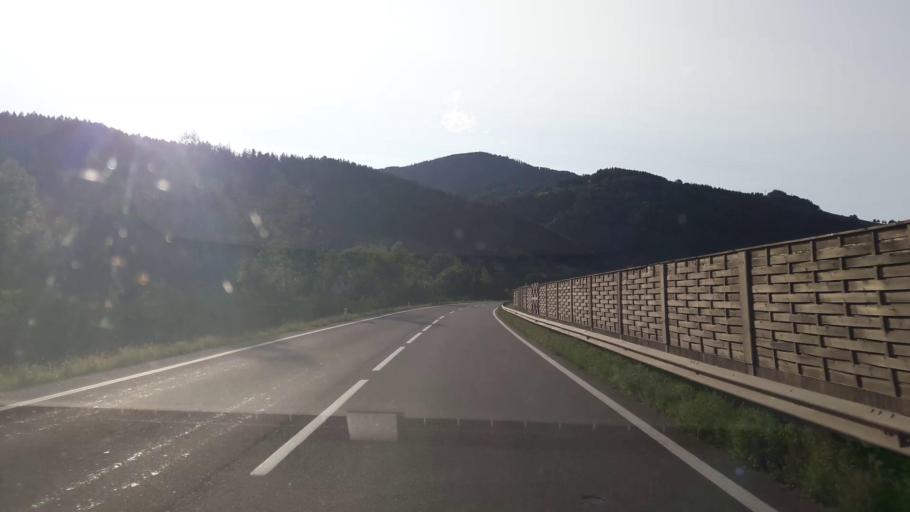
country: AT
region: Styria
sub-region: Politischer Bezirk Weiz
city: Anger
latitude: 47.2679
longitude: 15.6999
